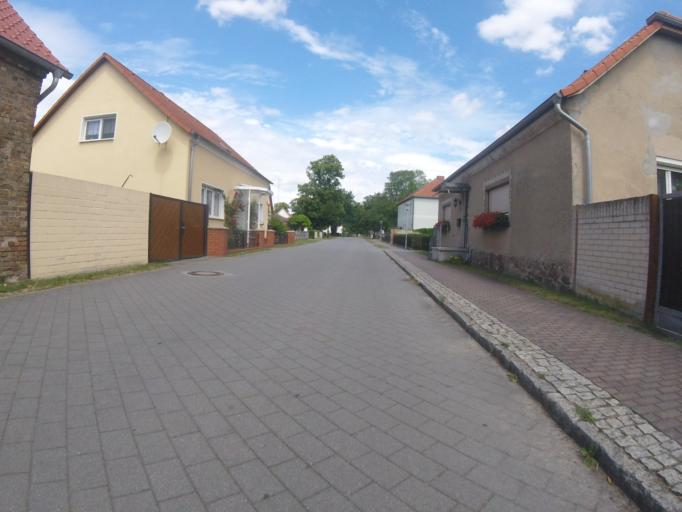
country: DE
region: Brandenburg
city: Bestensee
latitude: 52.2393
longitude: 13.7079
